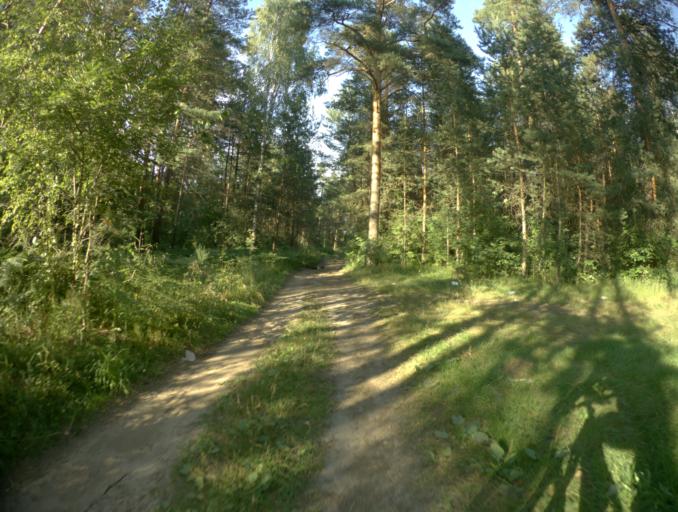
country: RU
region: Vladimir
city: Raduzhnyy
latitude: 56.0305
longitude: 40.4053
